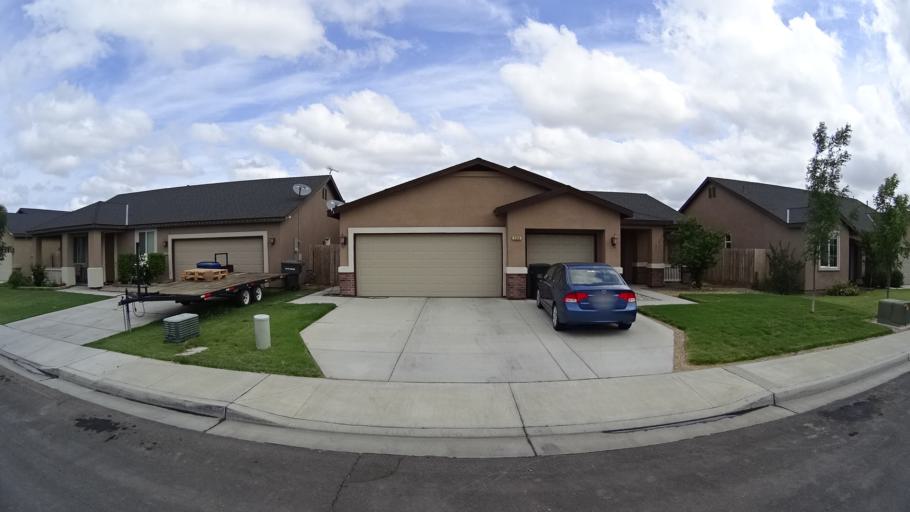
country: US
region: California
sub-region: Kings County
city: Hanford
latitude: 36.3091
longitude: -119.6650
